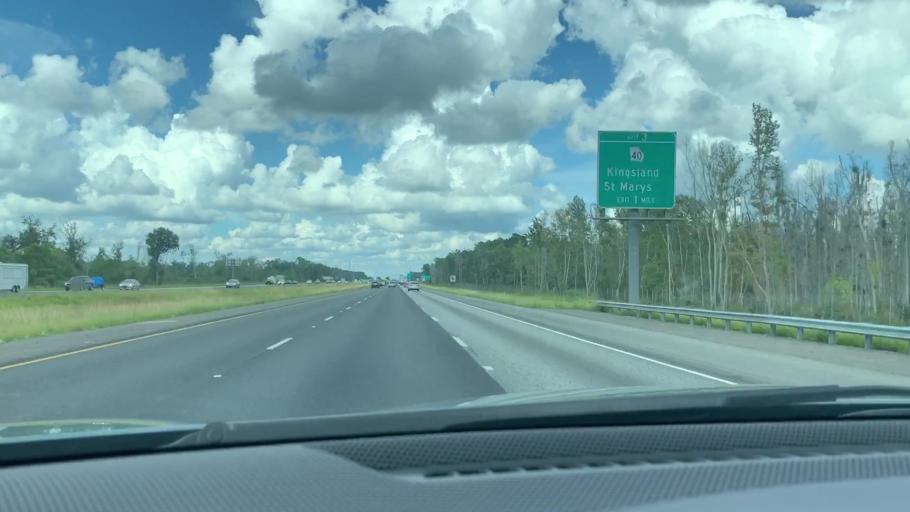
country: US
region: Georgia
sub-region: Camden County
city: Kingsland
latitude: 30.7754
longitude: -81.6555
